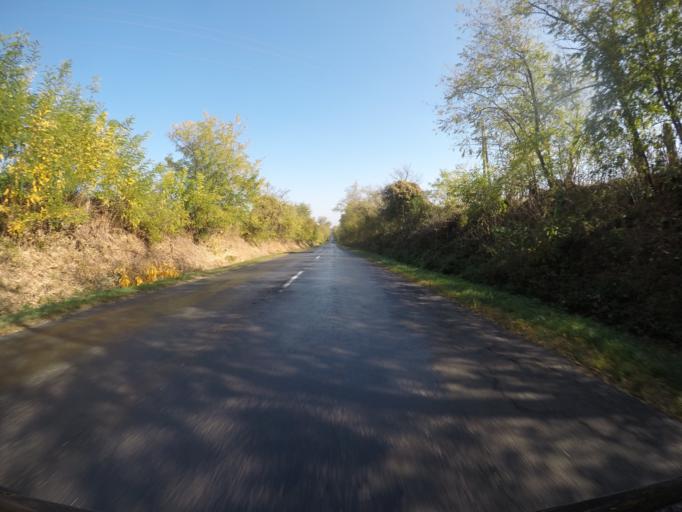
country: HU
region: Tolna
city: Dunaszentgyorgy
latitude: 46.6002
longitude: 18.7783
